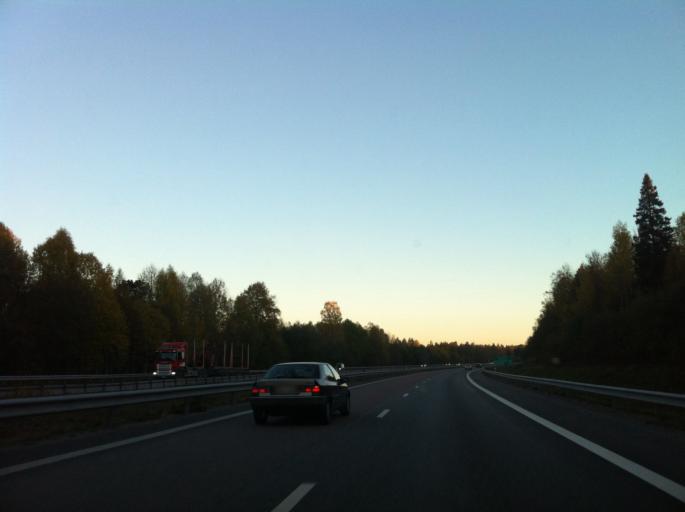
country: SE
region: Gaevleborg
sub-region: Gavle Kommun
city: Gavle
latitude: 60.6681
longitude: 17.0998
